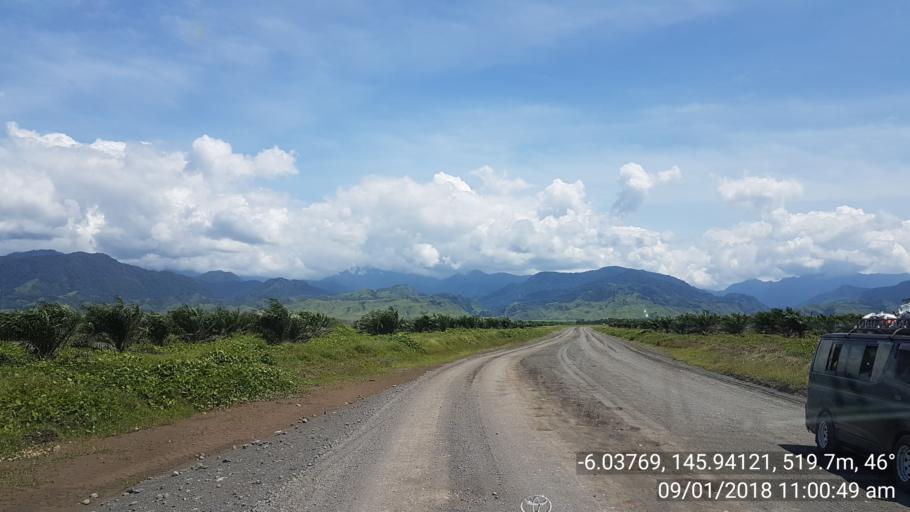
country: PG
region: Eastern Highlands
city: Kainantu
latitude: -6.0376
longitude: 145.9412
